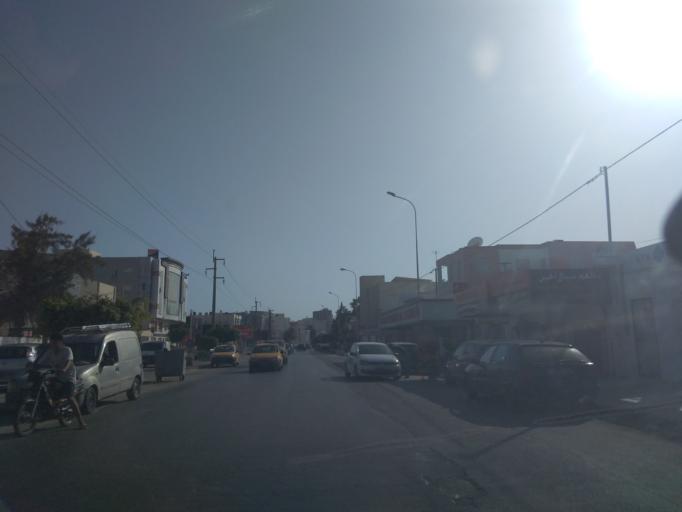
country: TN
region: Safaqis
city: Sfax
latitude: 34.7484
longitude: 10.7692
